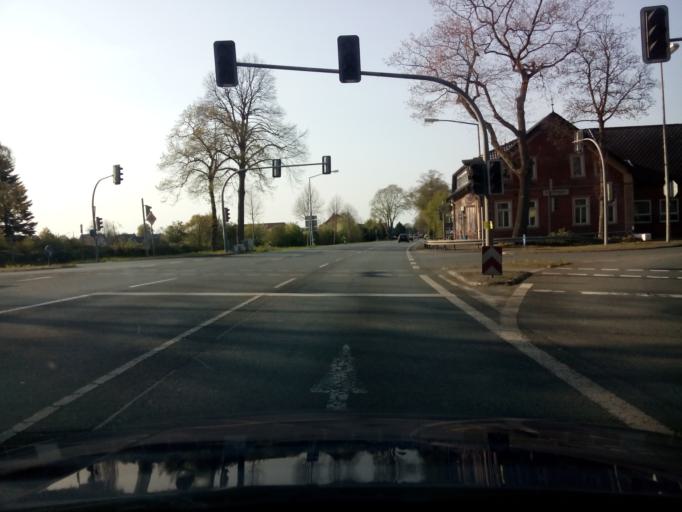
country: DE
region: Lower Saxony
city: Syke
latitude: 52.9626
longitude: 8.7994
